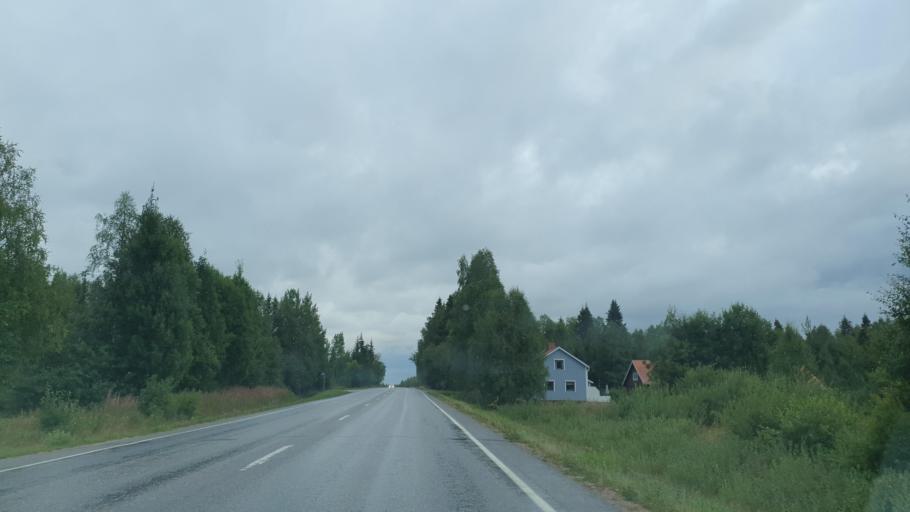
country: FI
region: Lapland
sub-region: Tunturi-Lappi
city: Kolari
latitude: 67.2302
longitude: 23.8928
